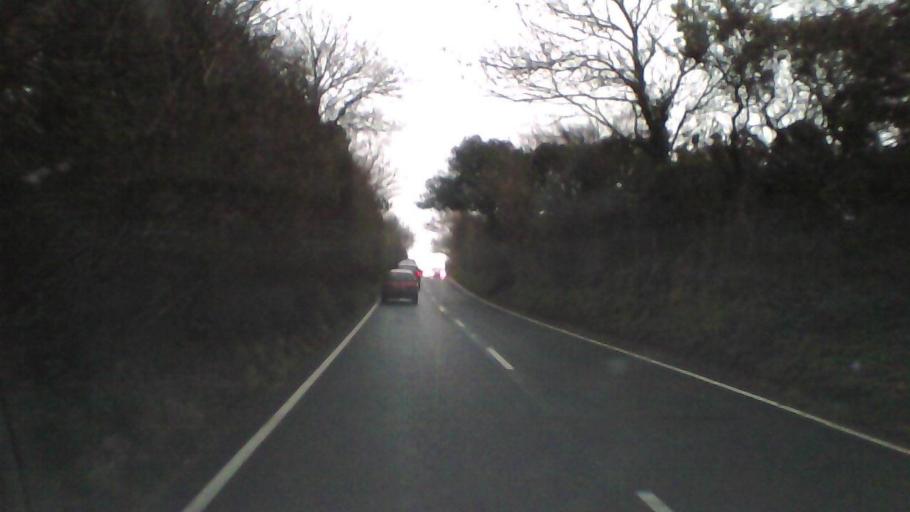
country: GB
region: England
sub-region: Isle of Wight
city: Newport
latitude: 50.6909
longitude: -1.2515
